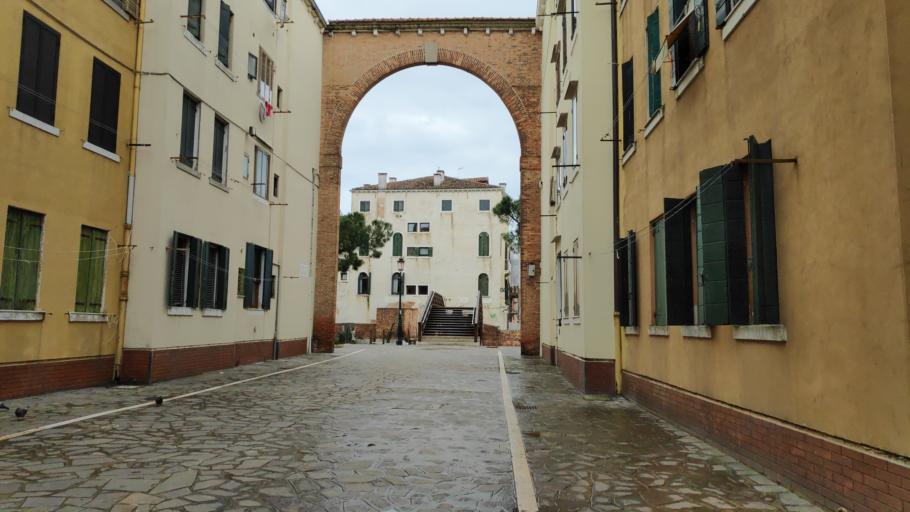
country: IT
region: Veneto
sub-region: Provincia di Venezia
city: Venice
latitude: 45.4473
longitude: 12.3210
